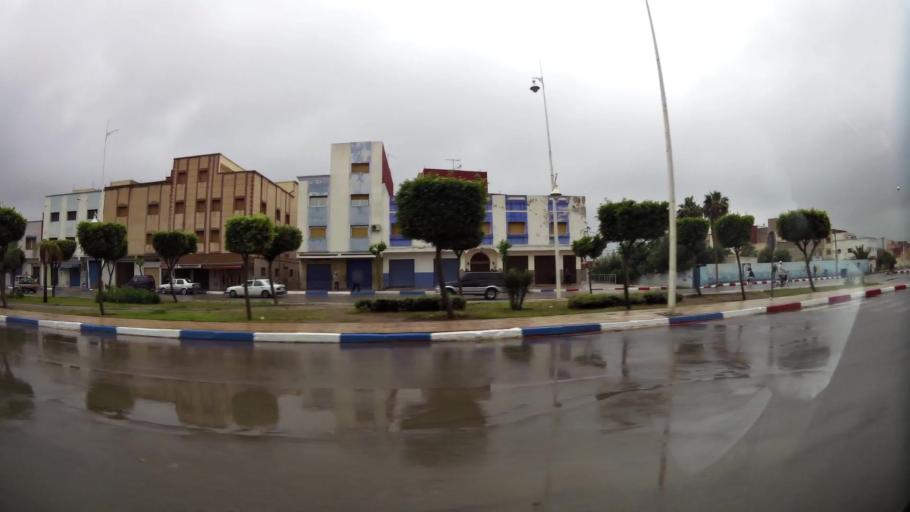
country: MA
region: Oriental
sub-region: Nador
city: Nador
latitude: 35.1661
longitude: -2.9505
